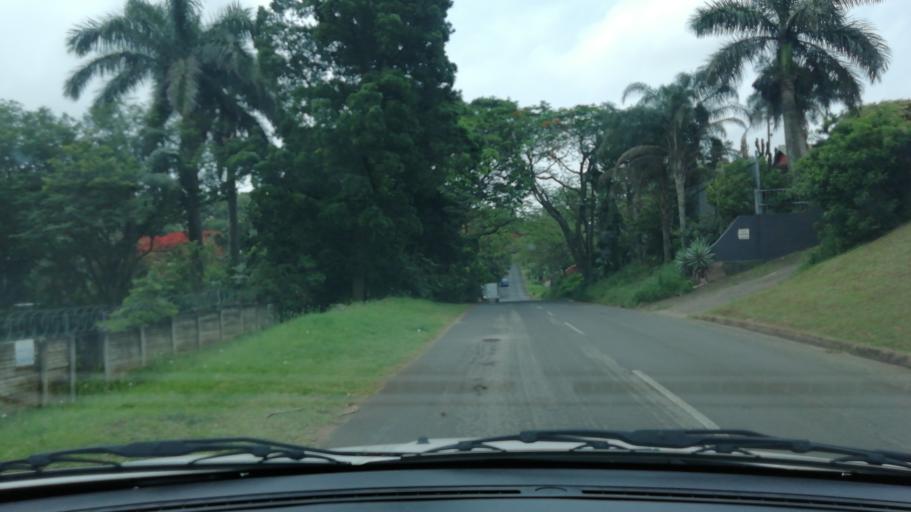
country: ZA
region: KwaZulu-Natal
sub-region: uThungulu District Municipality
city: Empangeni
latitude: -28.7531
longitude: 31.8923
